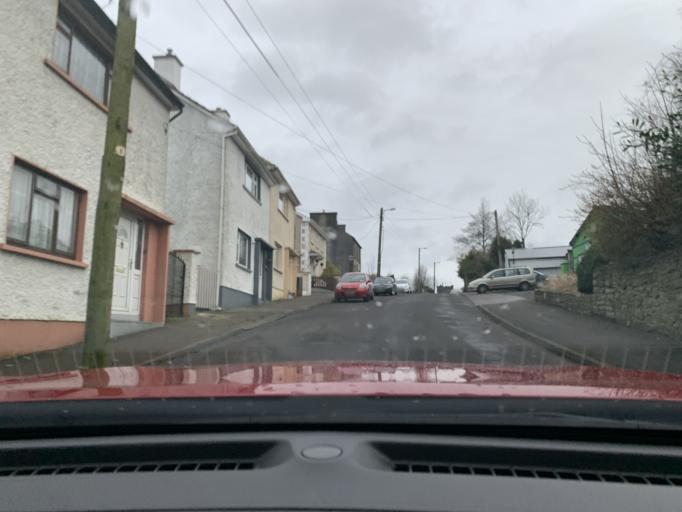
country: IE
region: Connaught
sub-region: Roscommon
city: Boyle
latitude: 53.9741
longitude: -8.3038
